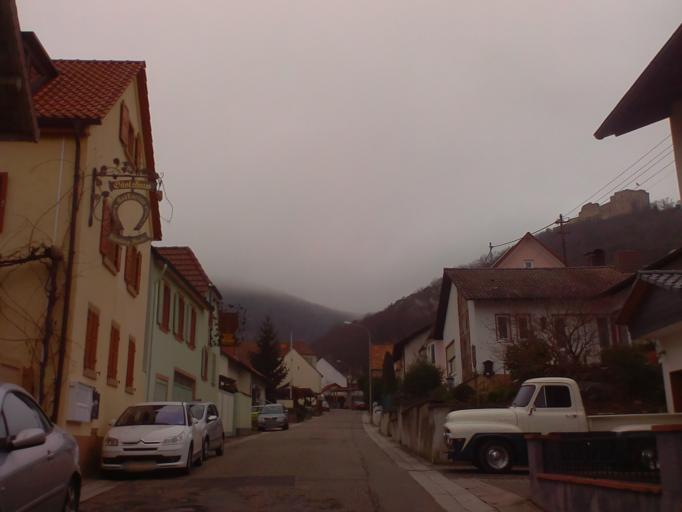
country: DE
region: Rheinland-Pfalz
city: Maikammer
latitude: 49.3224
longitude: 8.1254
